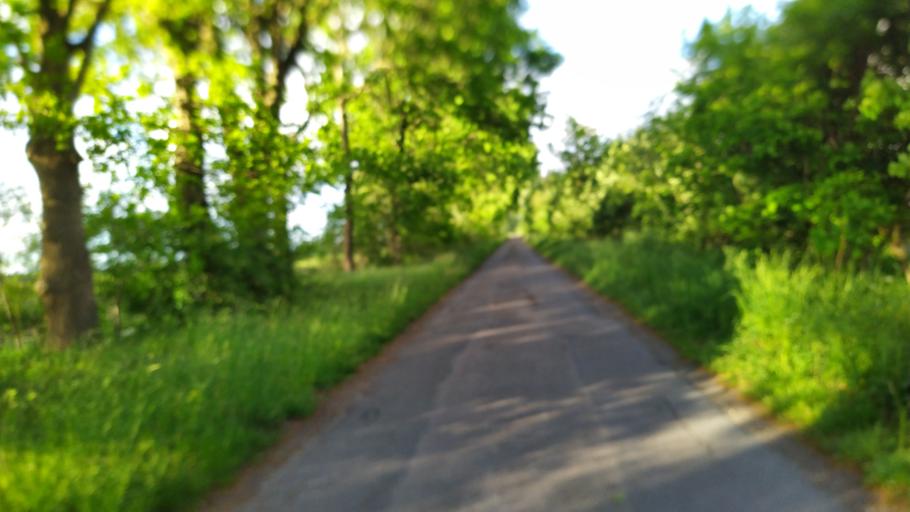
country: DE
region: Lower Saxony
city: Brest
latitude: 53.4695
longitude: 9.3960
